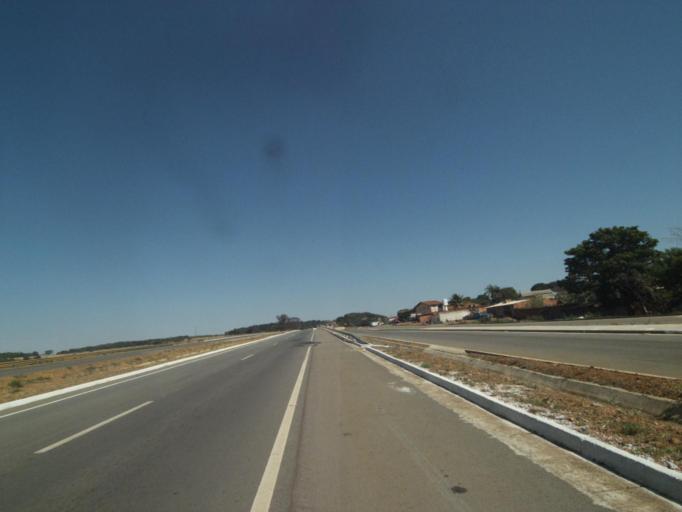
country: BR
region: Goias
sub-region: Anapolis
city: Anapolis
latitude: -16.1918
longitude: -49.0327
